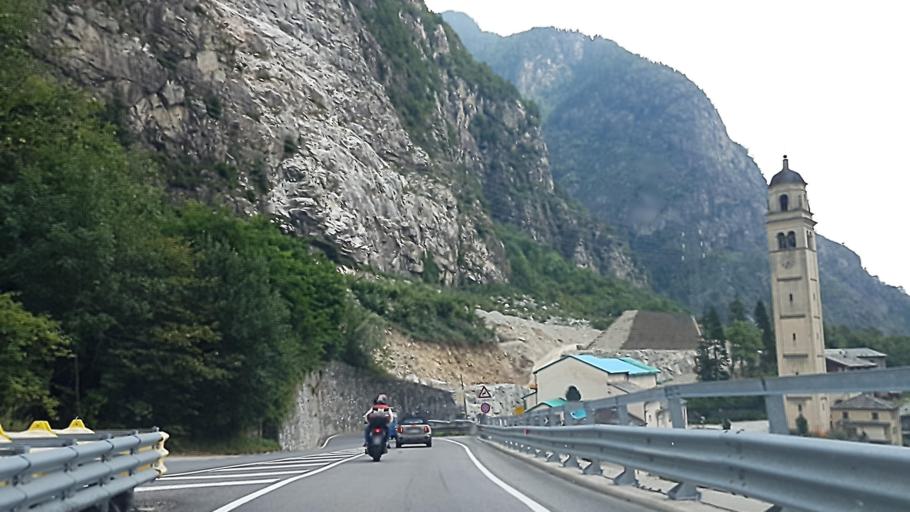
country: IT
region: Lombardy
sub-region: Provincia di Sondrio
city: San Giacomo Filippo
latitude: 46.3638
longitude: 9.3635
